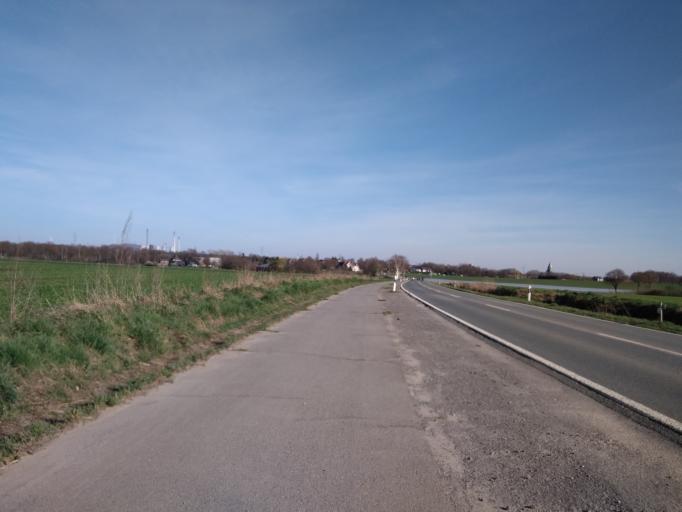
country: DE
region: North Rhine-Westphalia
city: Dorsten
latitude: 51.6122
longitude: 6.9057
